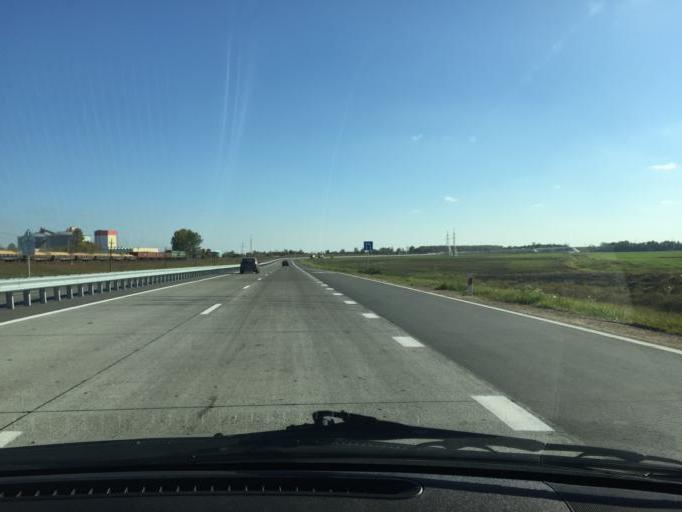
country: BY
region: Minsk
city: Slutsk
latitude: 53.0013
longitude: 27.4985
